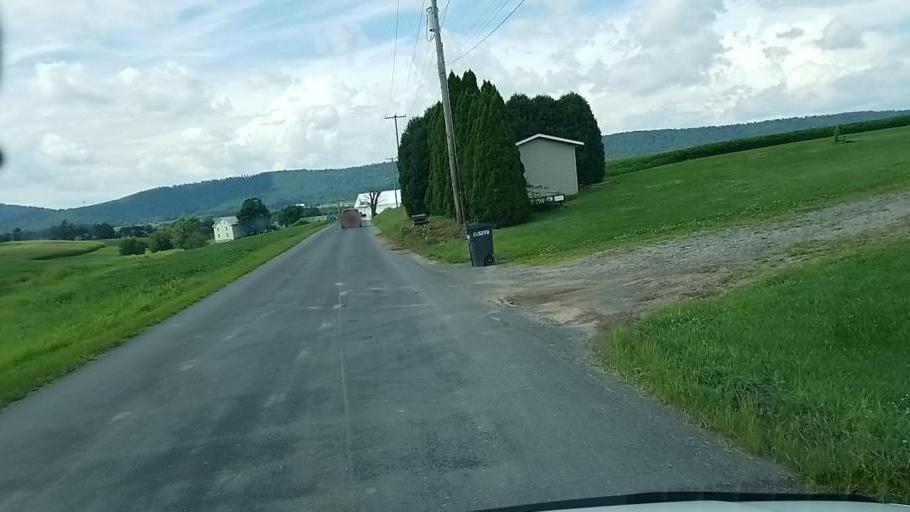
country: US
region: Pennsylvania
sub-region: Dauphin County
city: Elizabethville
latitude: 40.5875
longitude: -76.8444
